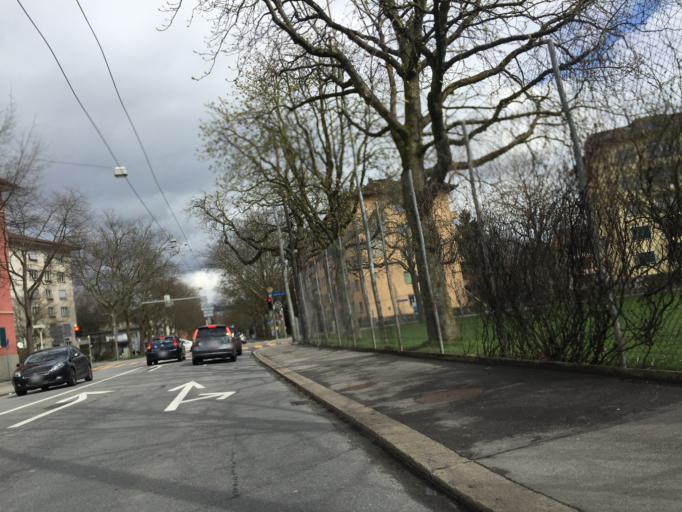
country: CH
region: Bern
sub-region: Bern-Mittelland District
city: Bern
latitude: 46.9630
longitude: 7.4540
